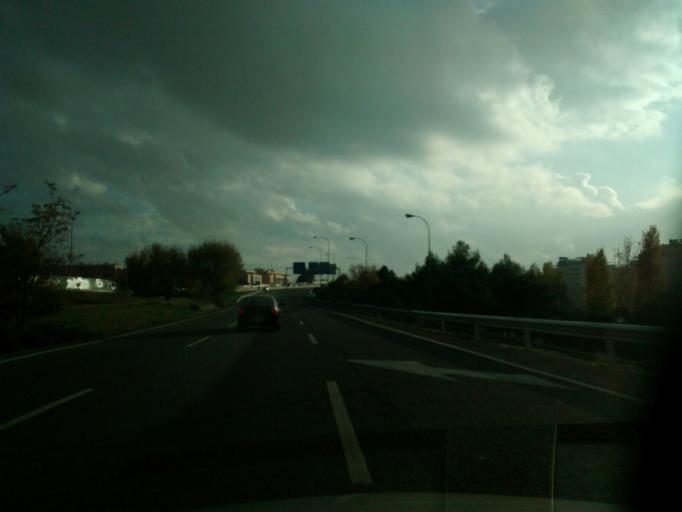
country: ES
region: Madrid
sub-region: Provincia de Madrid
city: San Blas
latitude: 40.4484
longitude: -3.5900
